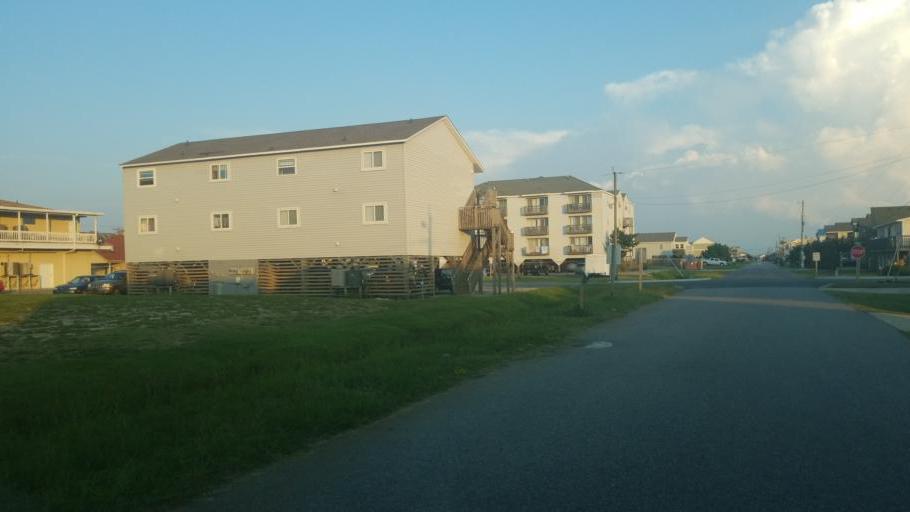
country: US
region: North Carolina
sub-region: Dare County
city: Kill Devil Hills
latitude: 36.0104
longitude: -75.6566
